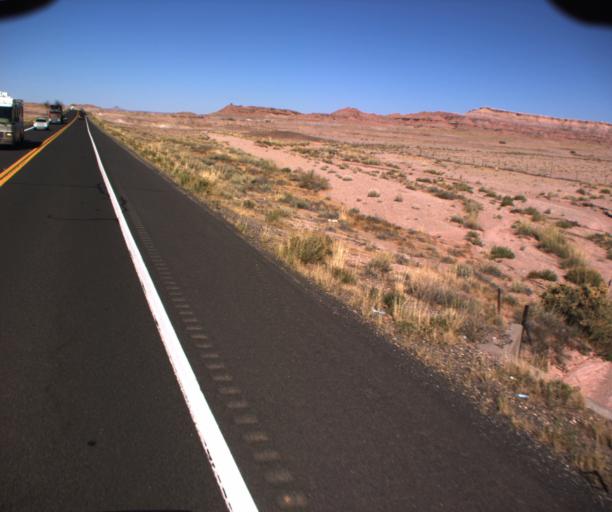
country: US
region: Arizona
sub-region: Coconino County
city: Tuba City
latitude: 35.9821
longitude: -111.3942
